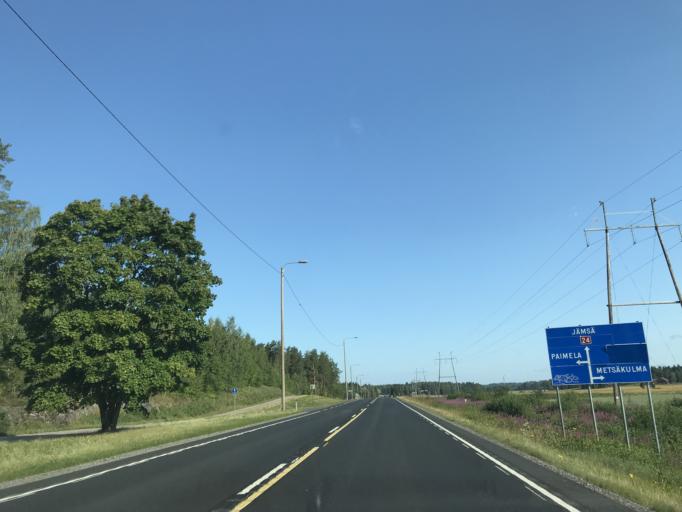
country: FI
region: Paijanne Tavastia
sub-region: Lahti
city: Lahti
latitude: 61.0886
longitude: 25.6514
